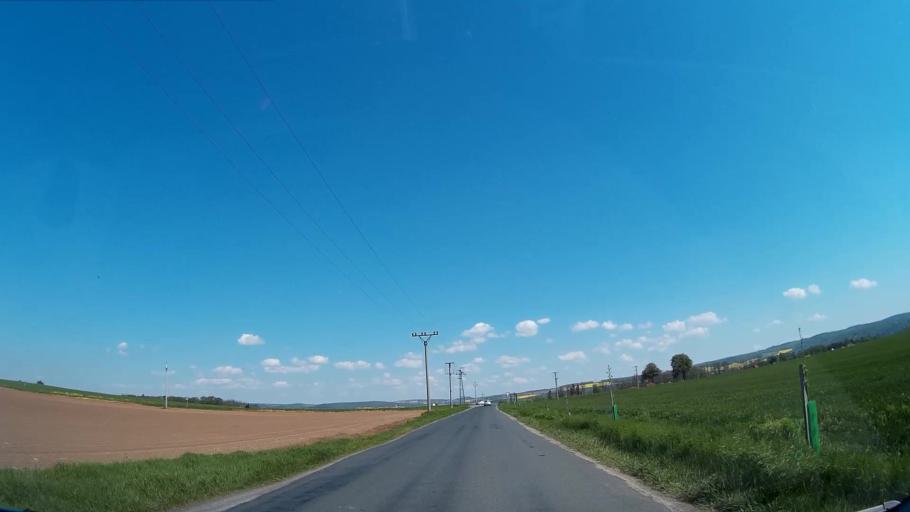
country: CZ
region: South Moravian
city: Ivancice
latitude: 49.0808
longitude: 16.3492
